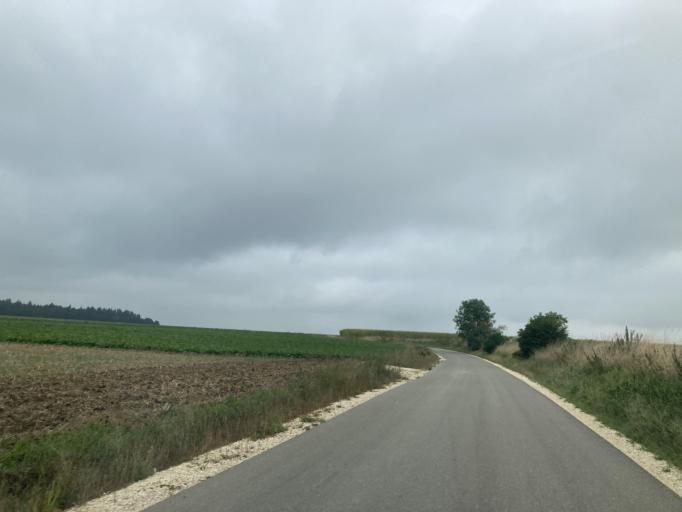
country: DE
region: Bavaria
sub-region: Swabia
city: Medlingen
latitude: 48.5752
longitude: 10.3070
